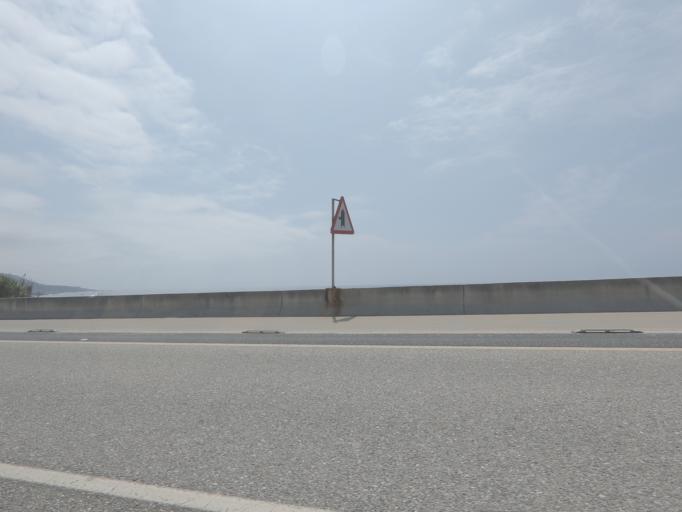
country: ES
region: Galicia
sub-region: Provincia de Pontevedra
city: Baiona
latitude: 42.1019
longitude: -8.8964
